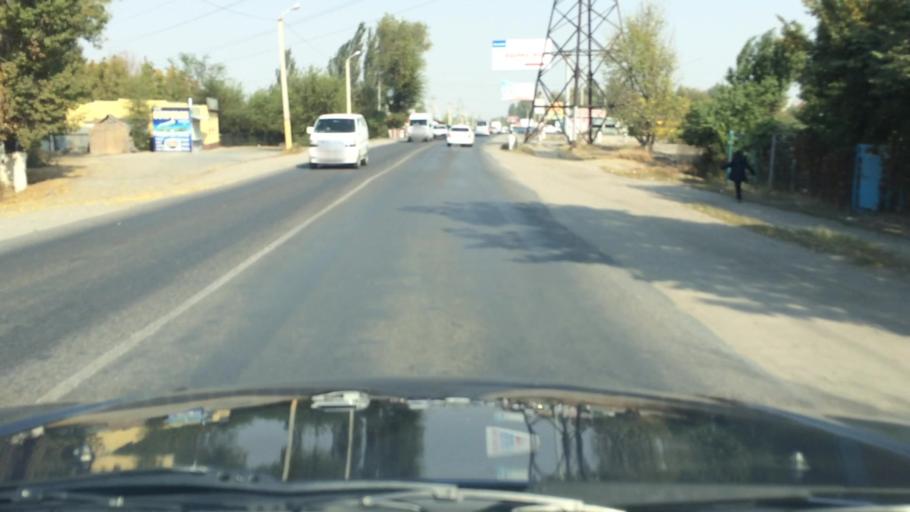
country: KG
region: Chuy
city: Lebedinovka
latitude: 42.8879
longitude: 74.6790
